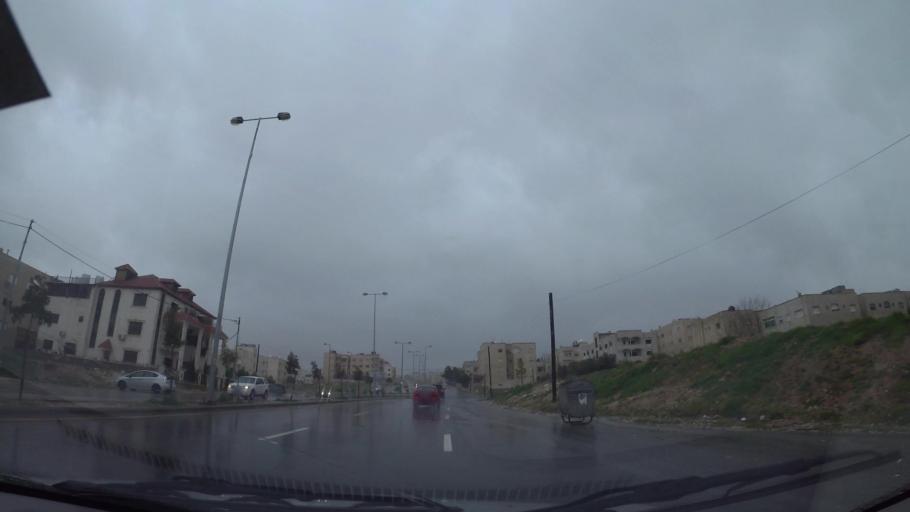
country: JO
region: Amman
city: Al Jubayhah
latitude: 32.0355
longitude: 35.8834
